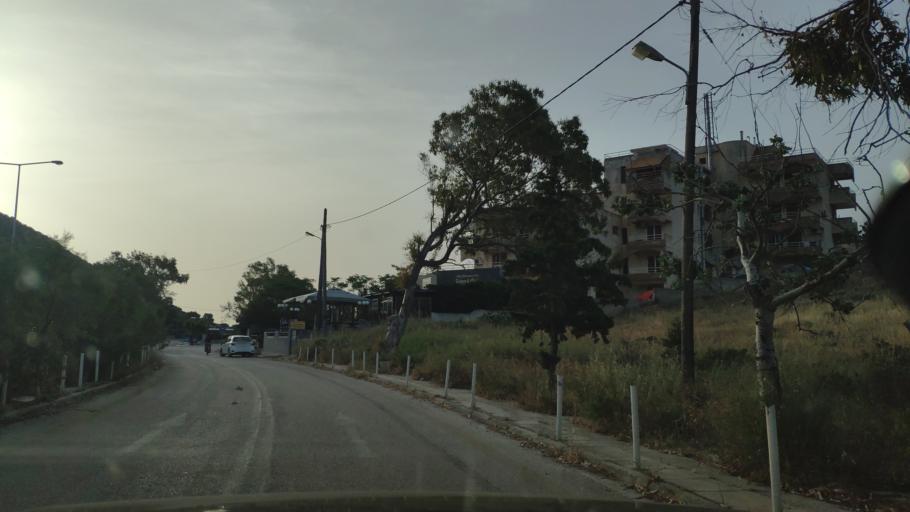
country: GR
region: Attica
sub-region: Nomarchia Anatolikis Attikis
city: Limin Mesoyaias
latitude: 37.8672
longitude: 24.0378
